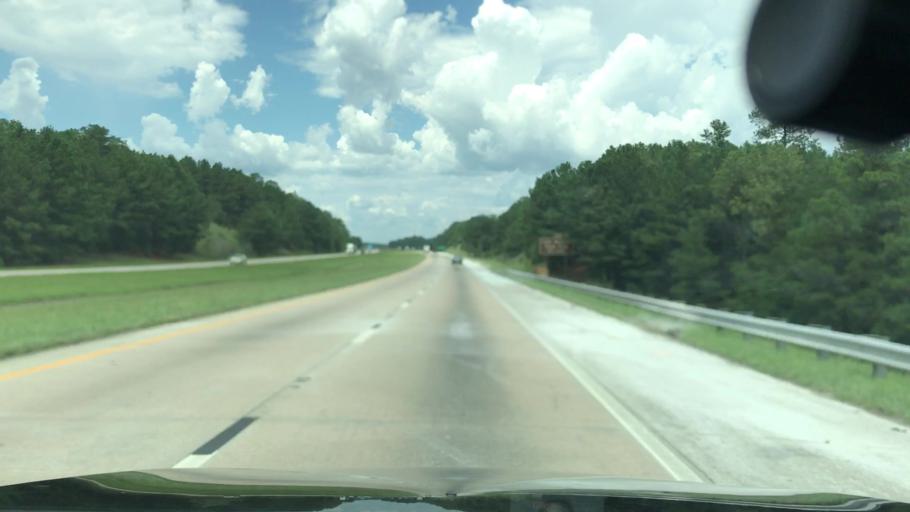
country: US
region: South Carolina
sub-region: Fairfield County
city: Winnsboro
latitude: 34.3944
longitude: -80.9937
